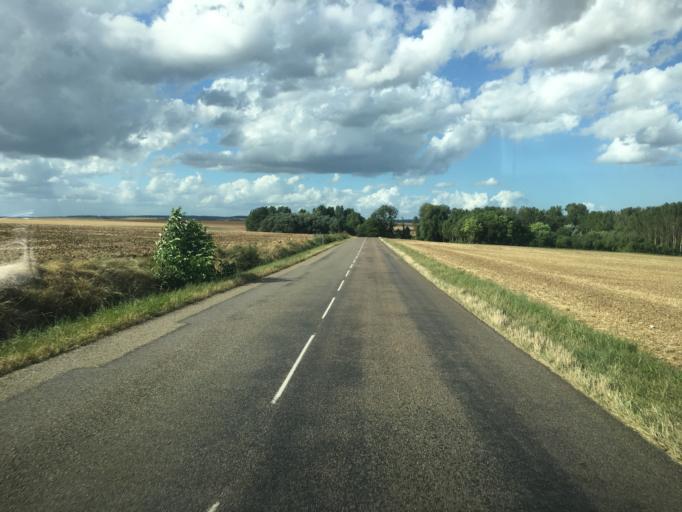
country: FR
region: Bourgogne
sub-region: Departement de l'Yonne
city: Laroche-Saint-Cydroine
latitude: 47.9329
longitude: 3.4370
